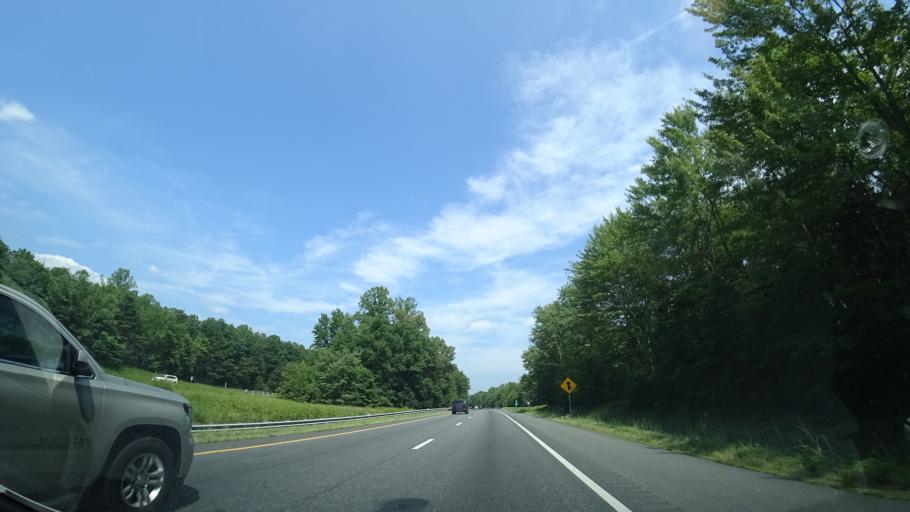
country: US
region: Virginia
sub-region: Fluvanna County
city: Lake Monticello
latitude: 37.9969
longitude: -78.3361
